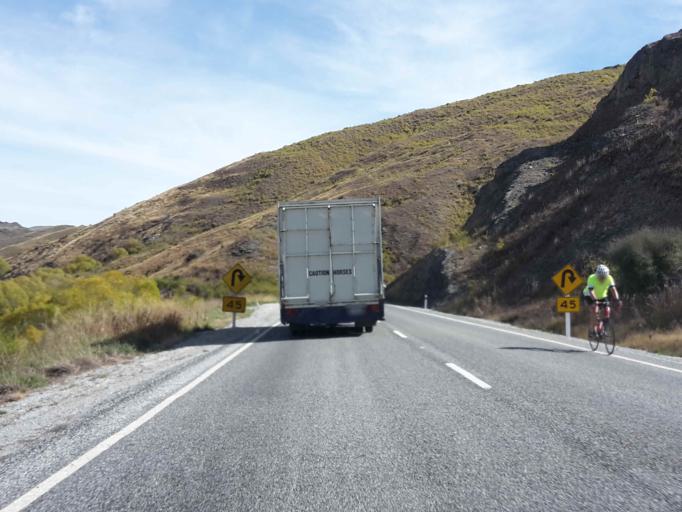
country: NZ
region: Otago
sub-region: Queenstown-Lakes District
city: Wanaka
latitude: -44.6954
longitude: 169.4878
